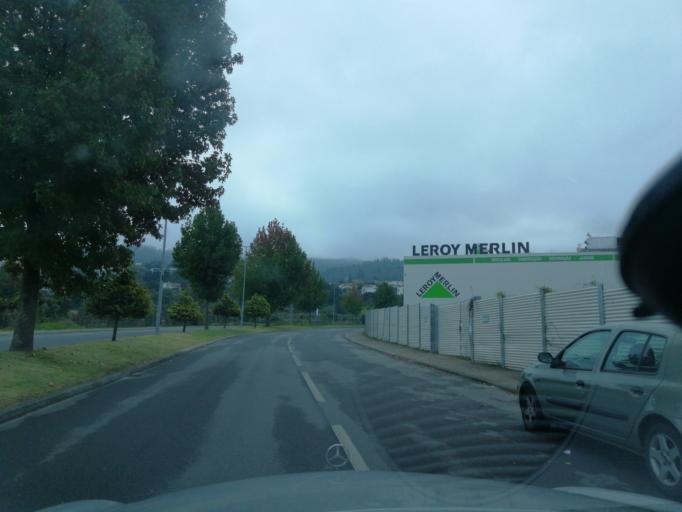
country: PT
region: Braga
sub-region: Braga
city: Braga
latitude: 41.5480
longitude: -8.3999
